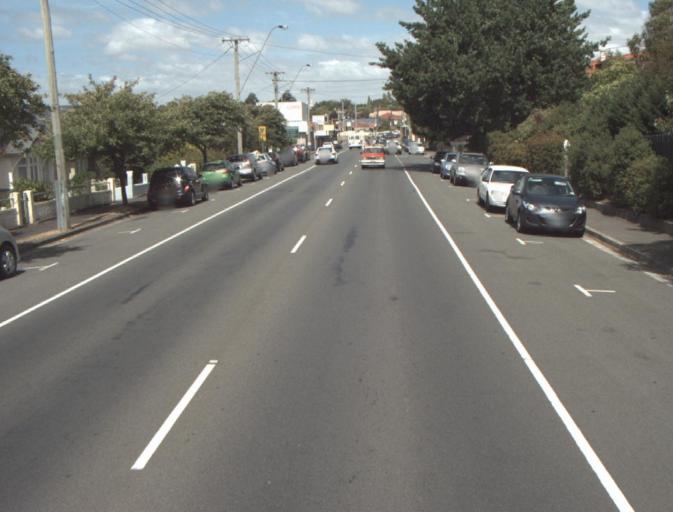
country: AU
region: Tasmania
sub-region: Launceston
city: East Launceston
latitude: -41.4401
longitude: 147.1598
